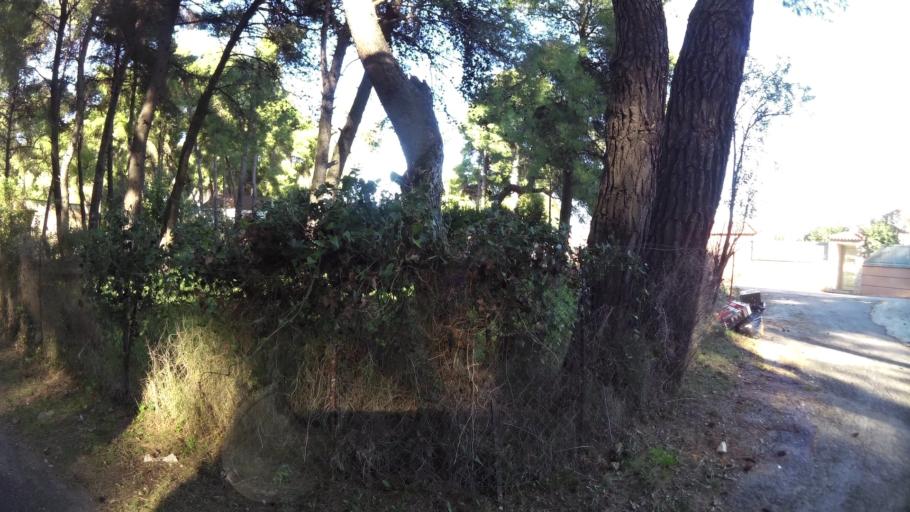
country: GR
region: Attica
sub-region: Nomarchia Anatolikis Attikis
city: Anoixi
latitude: 38.1252
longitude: 23.8498
